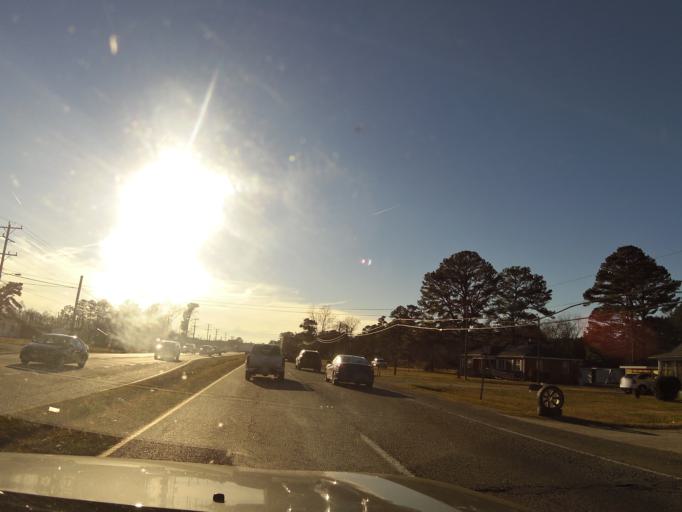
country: US
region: Virginia
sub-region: City of Suffolk
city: South Suffolk
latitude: 36.7177
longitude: -76.6578
